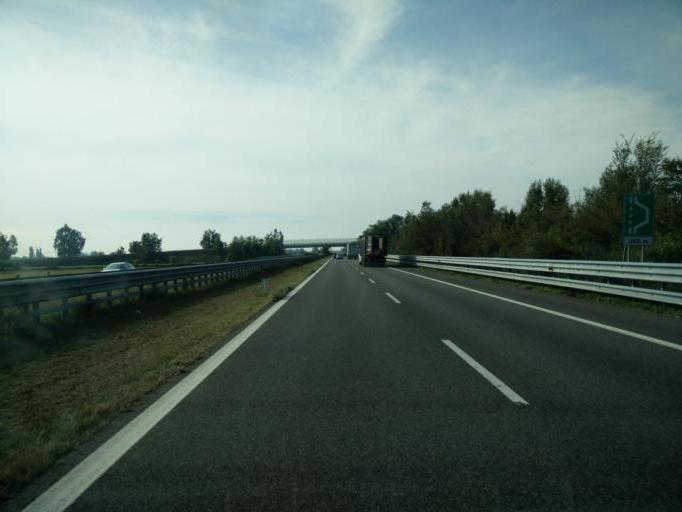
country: IT
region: Lombardy
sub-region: Provincia di Cremona
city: Dosimo
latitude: 45.1882
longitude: 10.0940
